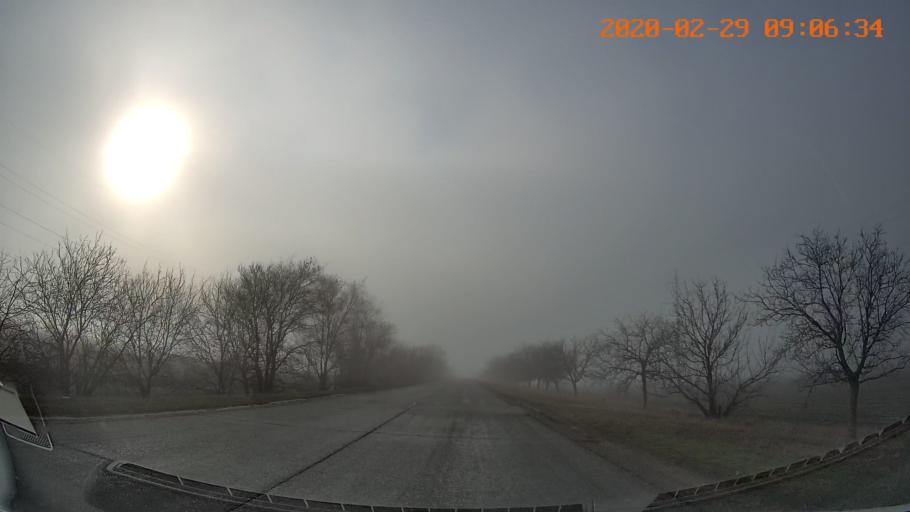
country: MD
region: Telenesti
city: Tiraspolul Nou
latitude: 46.8738
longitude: 29.7452
